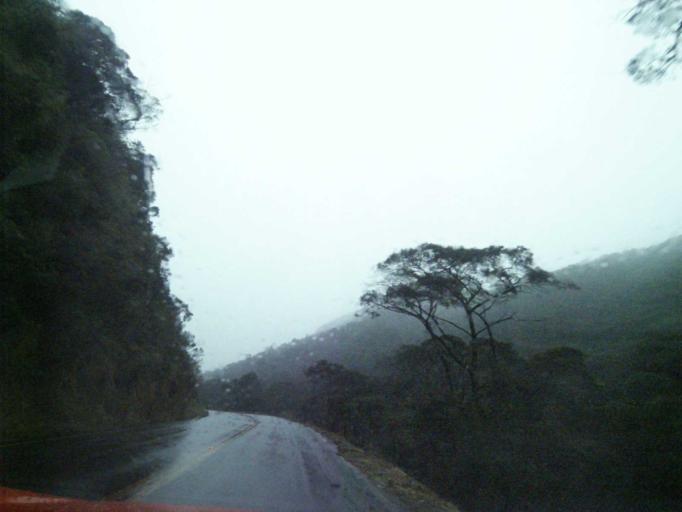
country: BR
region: Santa Catarina
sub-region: Anitapolis
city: Anitapolis
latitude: -27.7620
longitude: -49.0386
